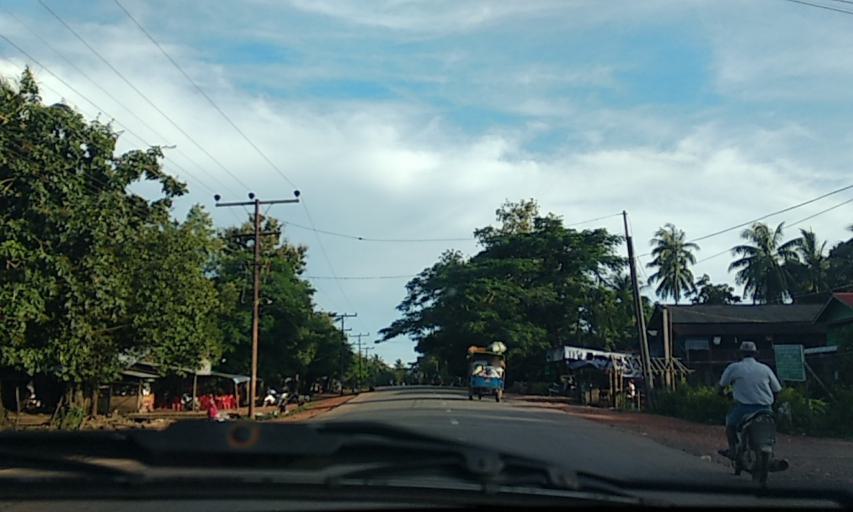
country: MM
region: Mon
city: Mawlamyine
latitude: 16.4092
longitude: 97.7008
